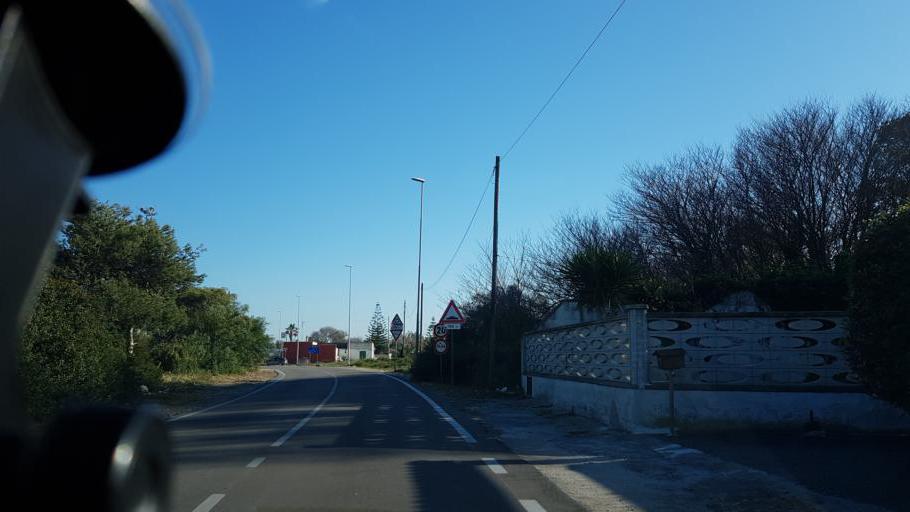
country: IT
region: Apulia
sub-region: Provincia di Lecce
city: Merine
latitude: 40.4288
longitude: 18.2426
